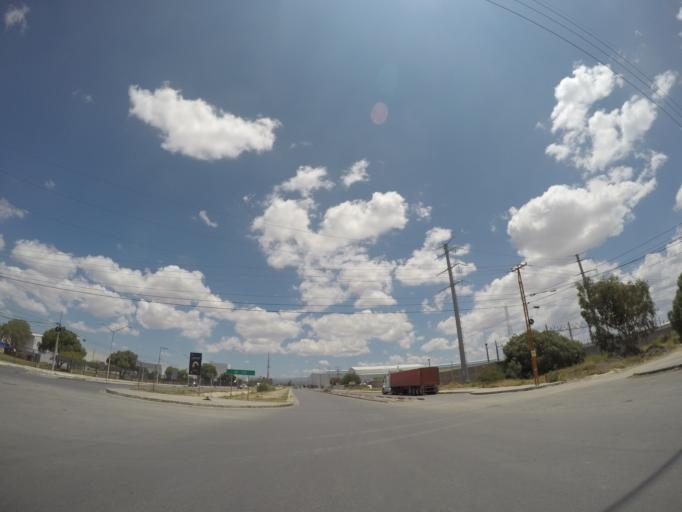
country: MX
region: San Luis Potosi
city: La Pila
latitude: 22.0490
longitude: -100.8696
